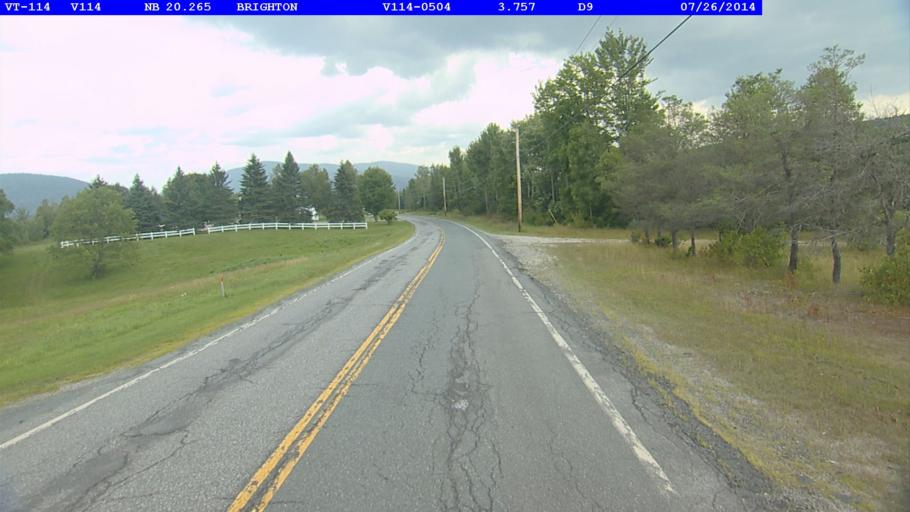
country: US
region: Vermont
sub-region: Caledonia County
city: Lyndonville
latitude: 44.7878
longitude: -71.9106
